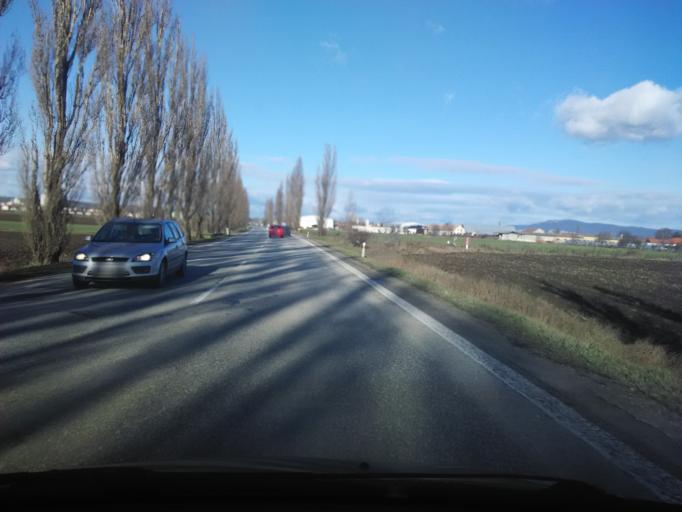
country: SK
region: Nitriansky
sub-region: Okres Nitra
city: Nitra
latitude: 48.2268
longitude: 18.1353
